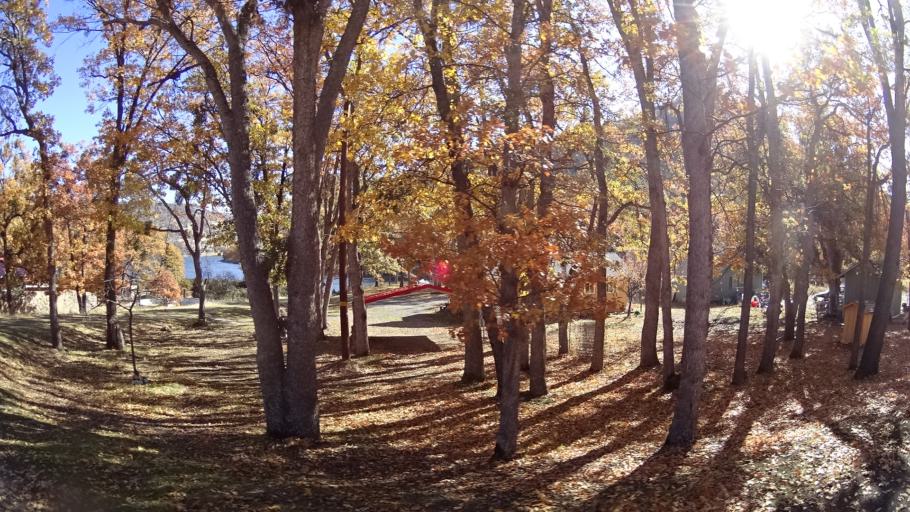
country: US
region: California
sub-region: Siskiyou County
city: Montague
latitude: 41.9735
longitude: -122.3025
